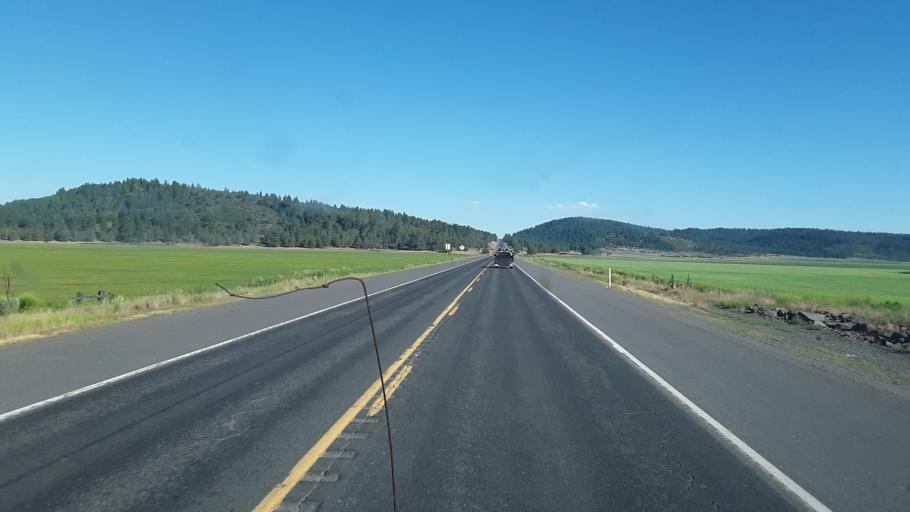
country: US
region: Oregon
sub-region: Klamath County
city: Klamath Falls
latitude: 42.2550
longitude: -121.8703
